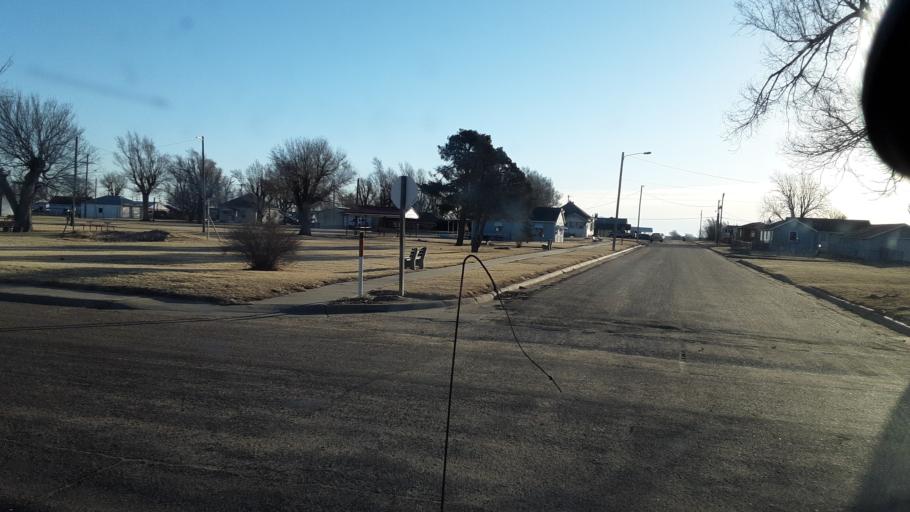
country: US
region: Kansas
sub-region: Rice County
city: Lyons
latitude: 38.3542
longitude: -98.3469
